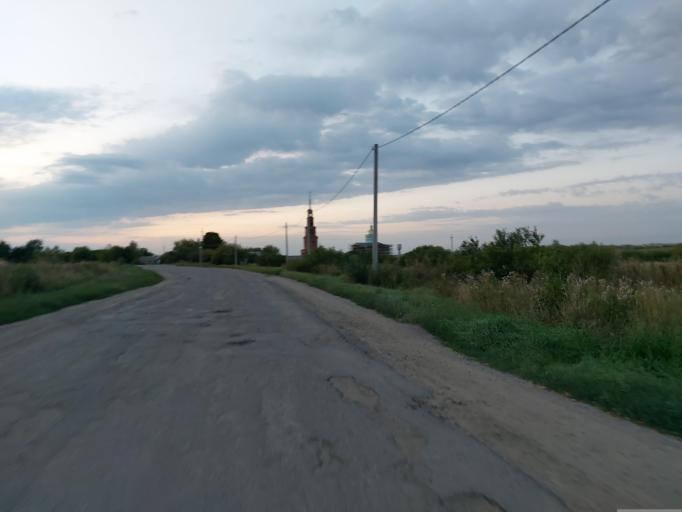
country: RU
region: Lipetsk
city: Dolgorukovo
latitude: 52.3743
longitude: 38.0530
